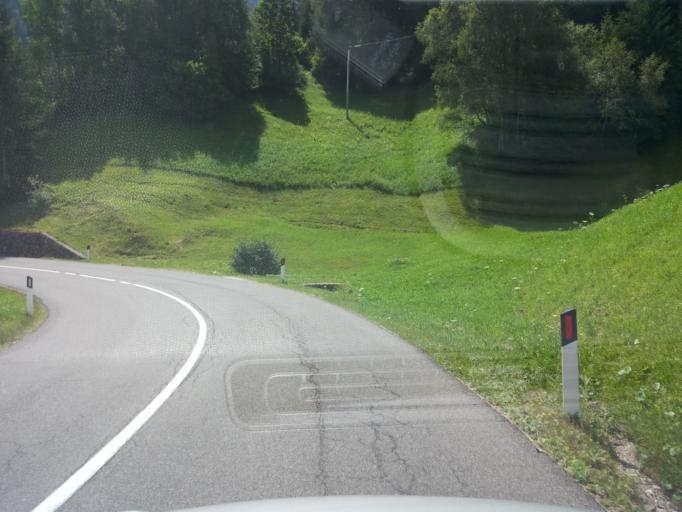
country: IT
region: Trentino-Alto Adige
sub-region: Bolzano
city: Ortisei
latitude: 46.5711
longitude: 11.6403
